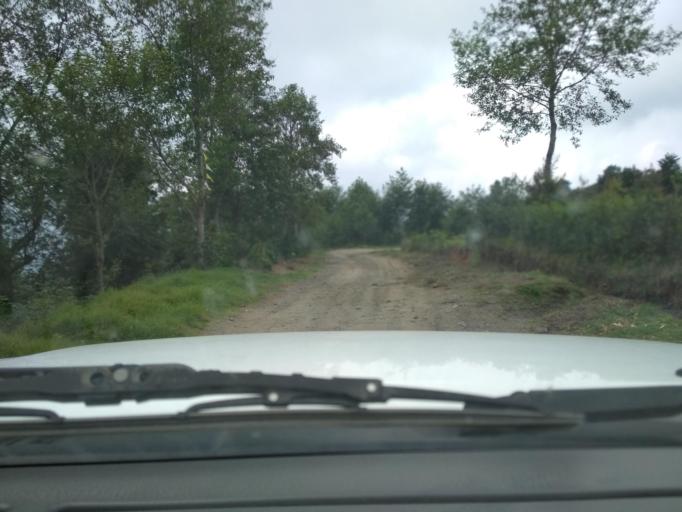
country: MX
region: Veracruz
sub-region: La Perla
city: Chilapa
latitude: 18.9907
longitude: -97.1630
